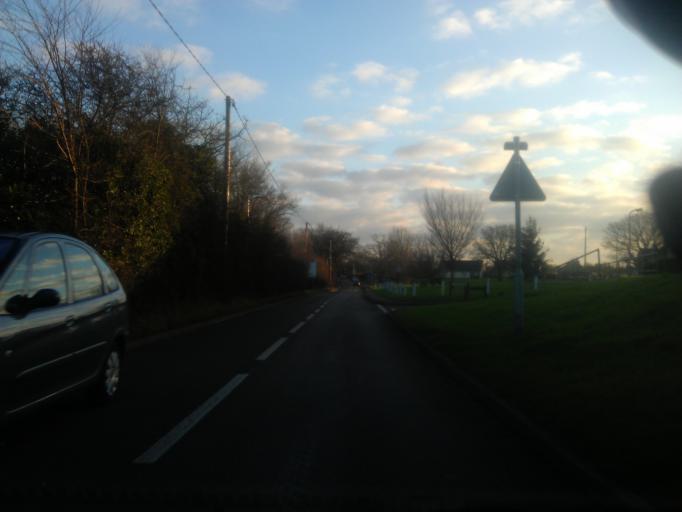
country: GB
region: England
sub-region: Essex
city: Witham
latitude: 51.8261
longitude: 0.6528
